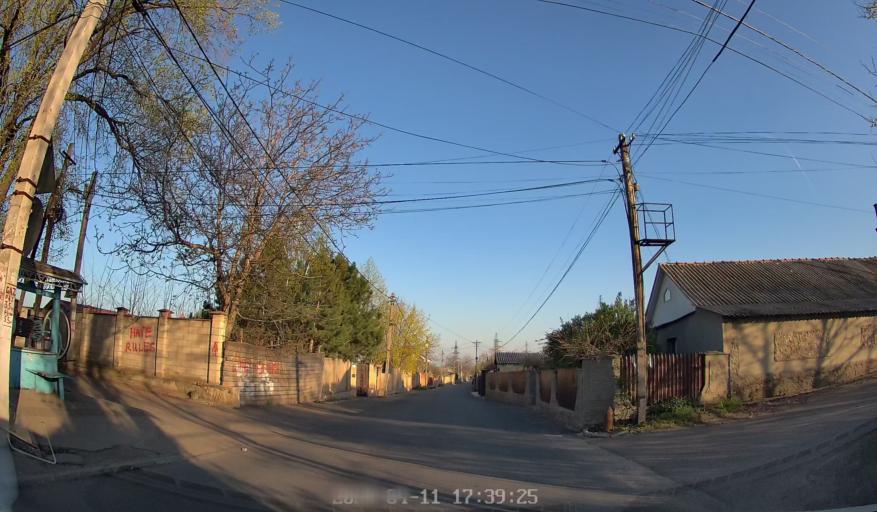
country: MD
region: Laloveni
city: Ialoveni
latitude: 46.9837
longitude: 28.8059
